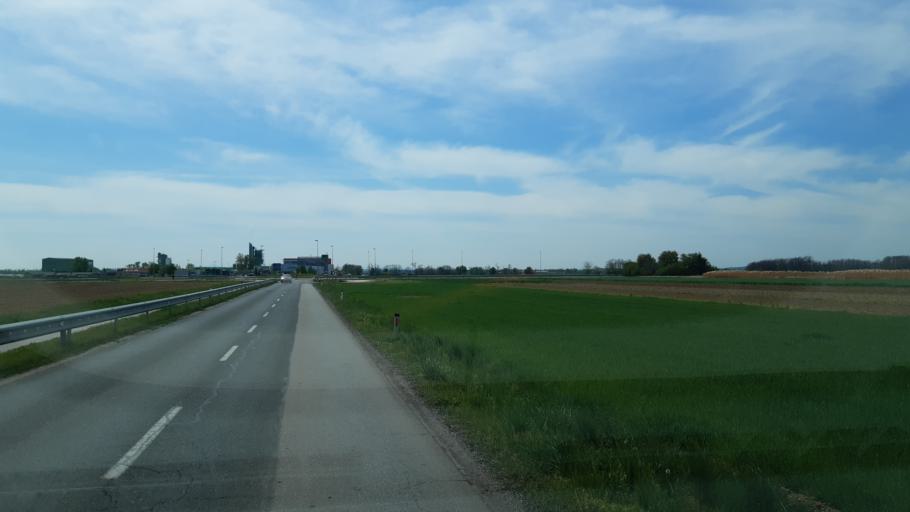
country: SI
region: Murska Sobota
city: Murska Sobota
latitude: 46.6494
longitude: 16.1684
